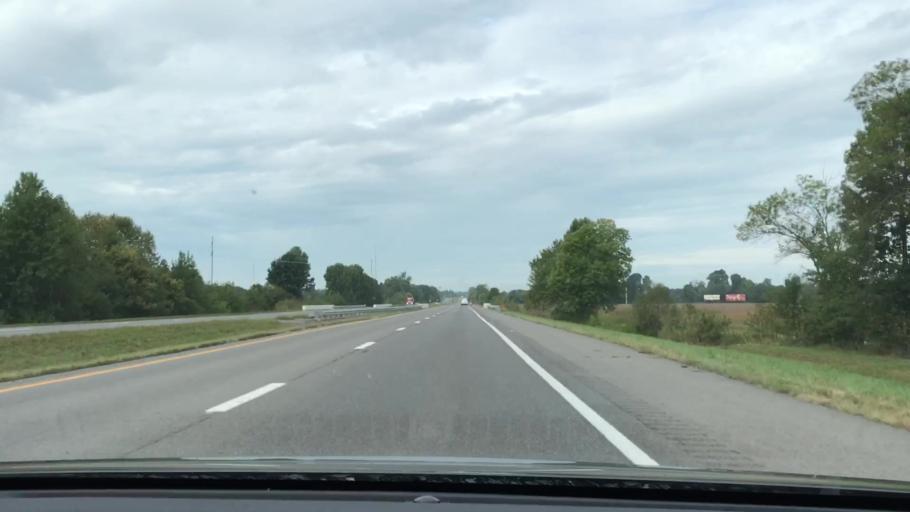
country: US
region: Kentucky
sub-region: Graves County
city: Mayfield
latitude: 36.7696
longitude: -88.6216
